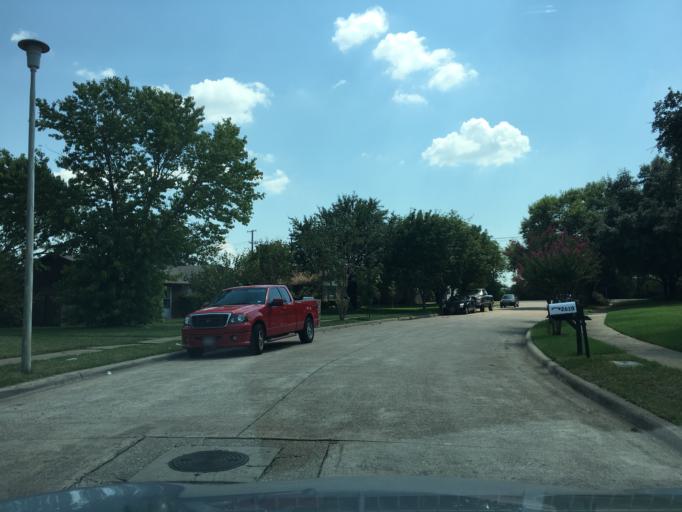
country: US
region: Texas
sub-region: Dallas County
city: Garland
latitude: 32.9623
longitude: -96.6684
